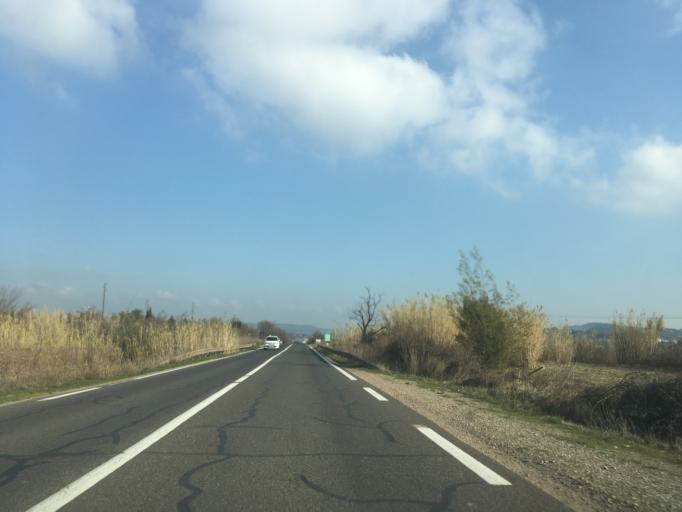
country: FR
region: Provence-Alpes-Cote d'Azur
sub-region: Departement du Var
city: Vidauban
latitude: 43.4090
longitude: 6.4137
